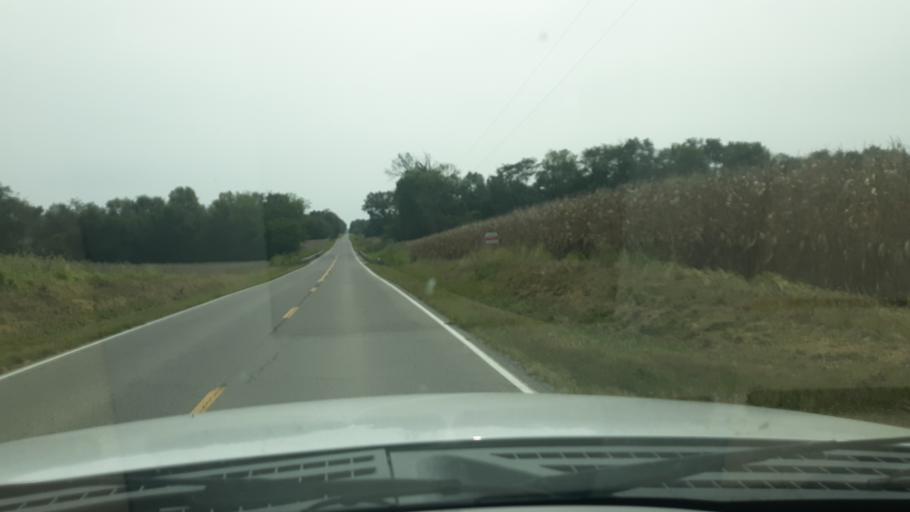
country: US
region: Illinois
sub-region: Saline County
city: Eldorado
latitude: 37.8558
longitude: -88.5305
